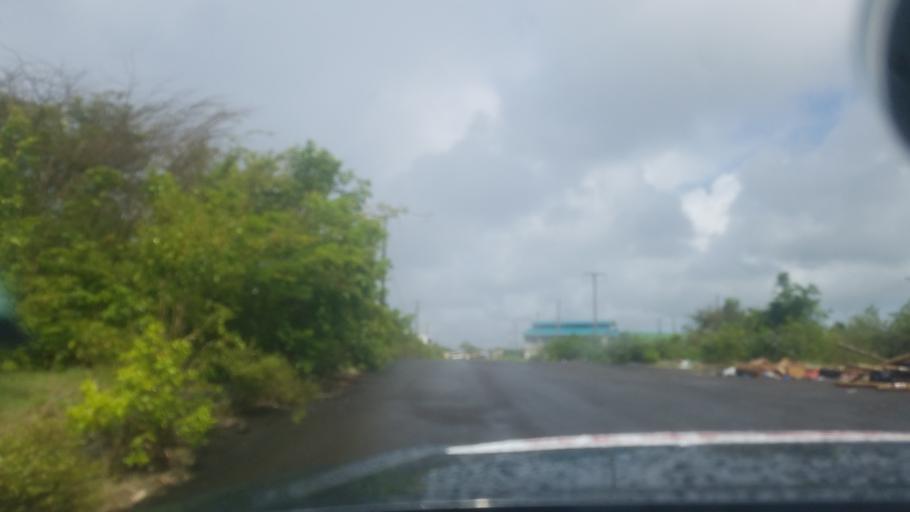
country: LC
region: Laborie Quarter
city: Laborie
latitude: 13.7361
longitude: -60.9719
